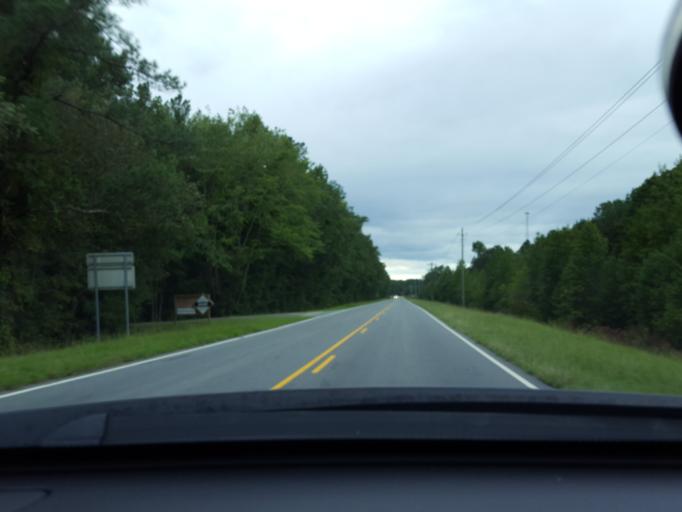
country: US
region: North Carolina
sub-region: Sampson County
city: Roseboro
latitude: 34.7613
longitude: -78.4092
